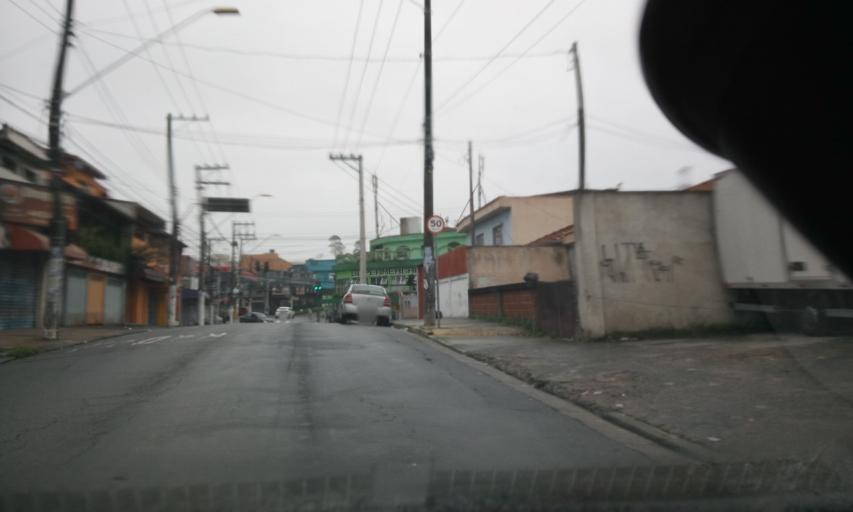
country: BR
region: Sao Paulo
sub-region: Santo Andre
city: Santo Andre
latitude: -23.7007
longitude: -46.5182
